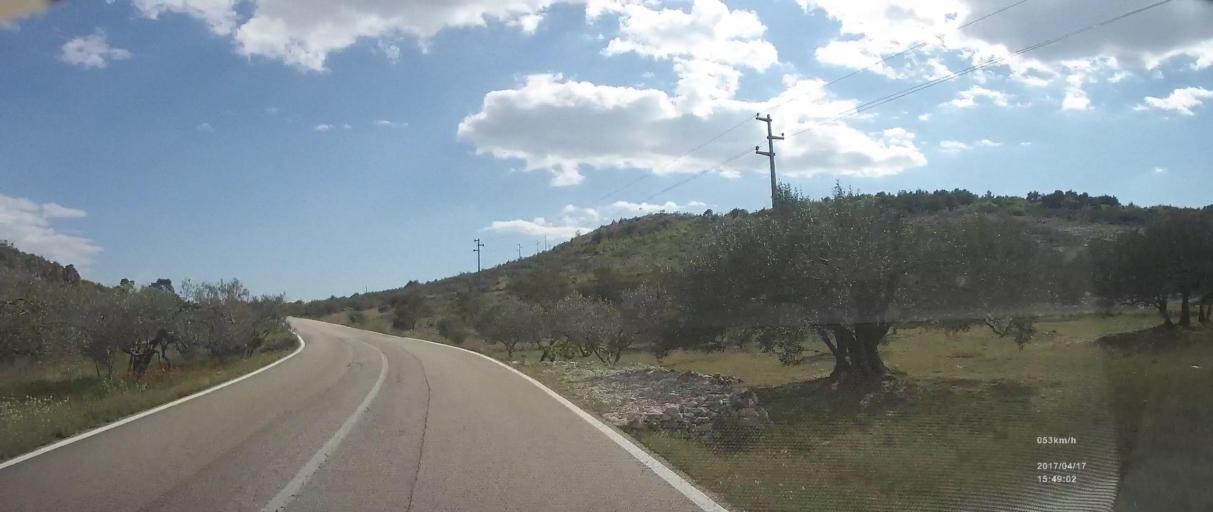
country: HR
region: Sibensko-Kniniska
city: Primosten
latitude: 43.6174
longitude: 15.9765
